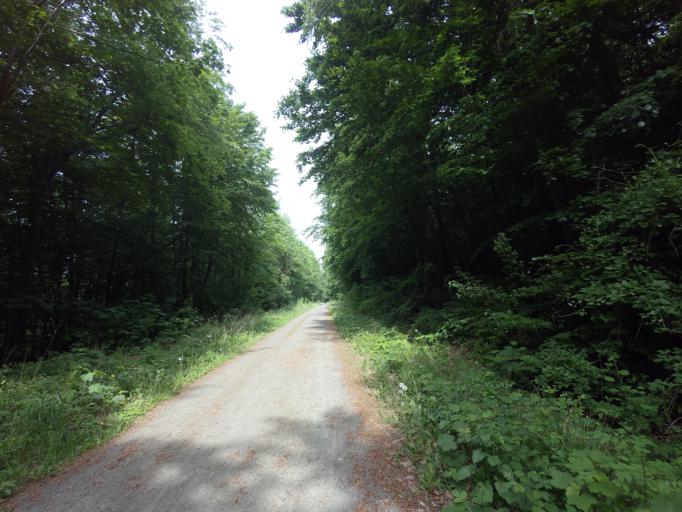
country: DE
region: Lower Saxony
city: Evessen
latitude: 52.1996
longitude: 10.7241
